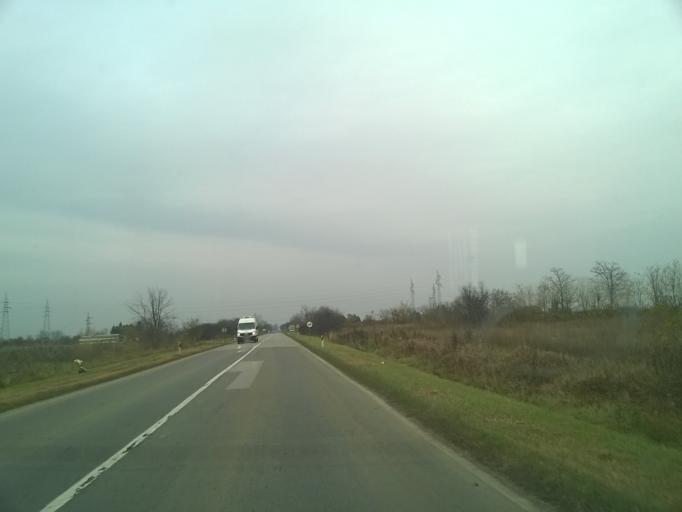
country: RS
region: Autonomna Pokrajina Vojvodina
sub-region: Juznobanatski Okrug
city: Pancevo
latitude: 44.9189
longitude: 20.6579
